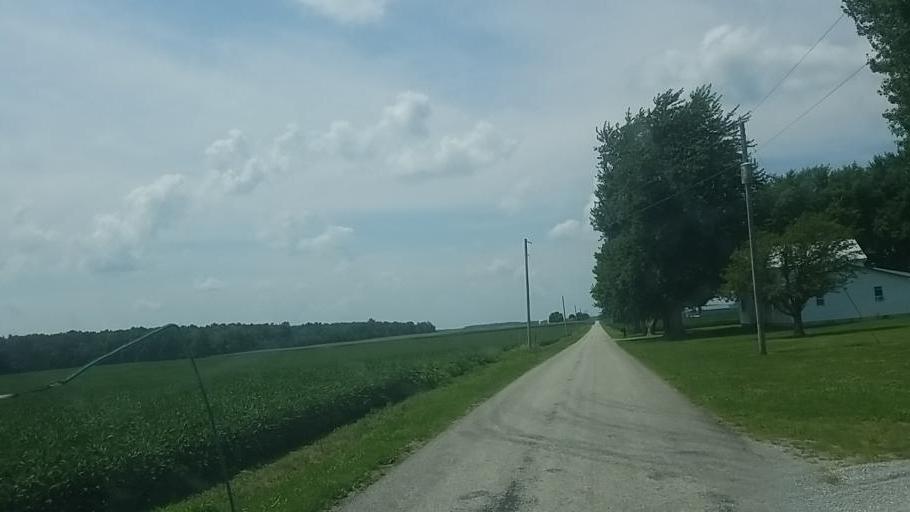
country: US
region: Ohio
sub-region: Marion County
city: Marion
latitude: 40.6733
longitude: -83.2500
